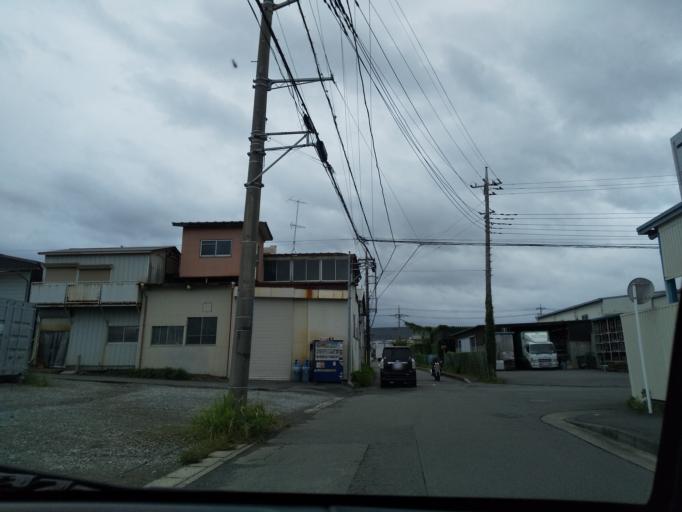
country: JP
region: Kanagawa
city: Minami-rinkan
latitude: 35.4398
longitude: 139.4388
